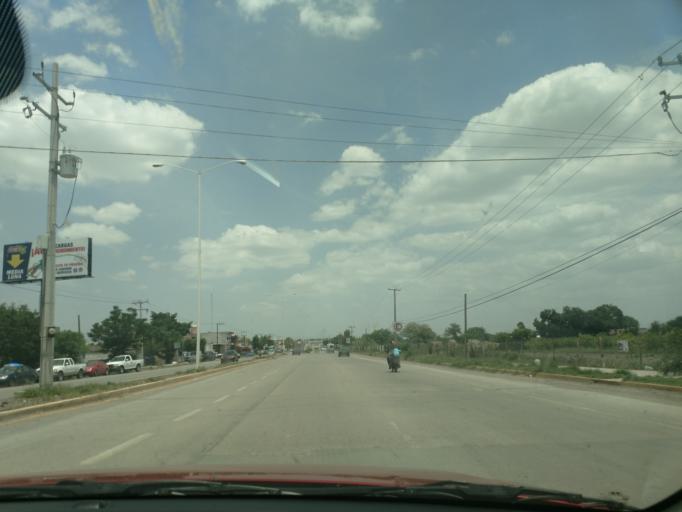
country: MX
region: San Luis Potosi
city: Ciudad Fernandez
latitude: 21.9353
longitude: -100.0260
